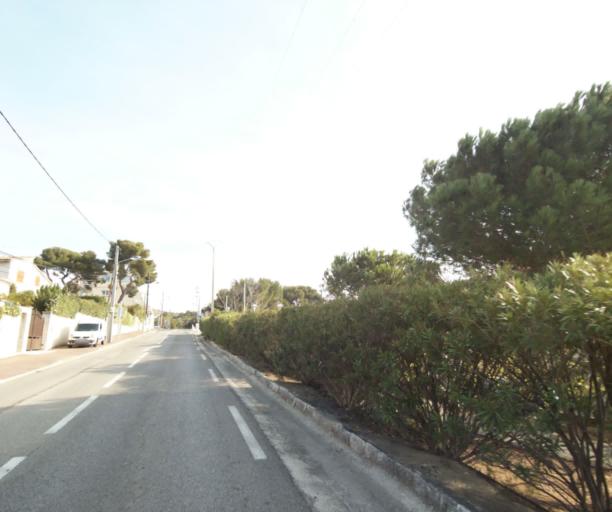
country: FR
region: Provence-Alpes-Cote d'Azur
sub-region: Departement des Bouches-du-Rhone
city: Carry-le-Rouet
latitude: 43.3358
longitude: 5.1526
